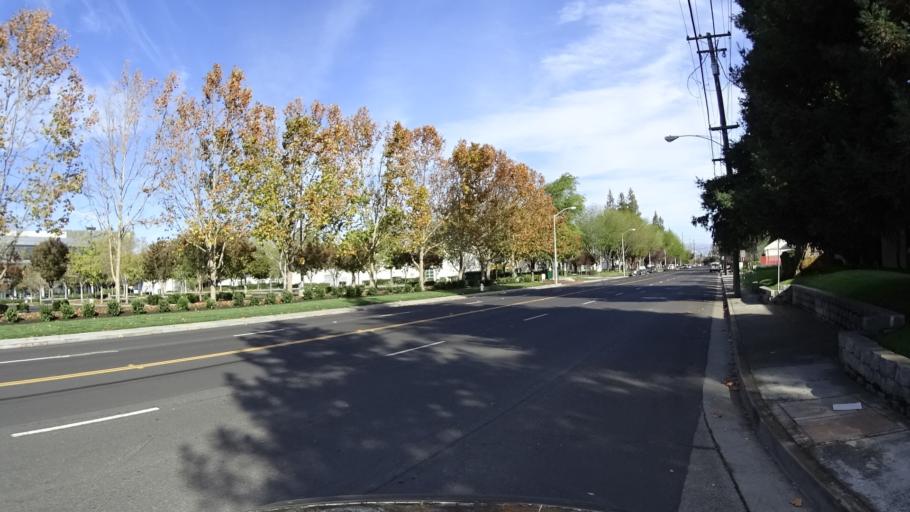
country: US
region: California
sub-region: Santa Clara County
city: Santa Clara
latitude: 37.3694
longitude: -121.9634
